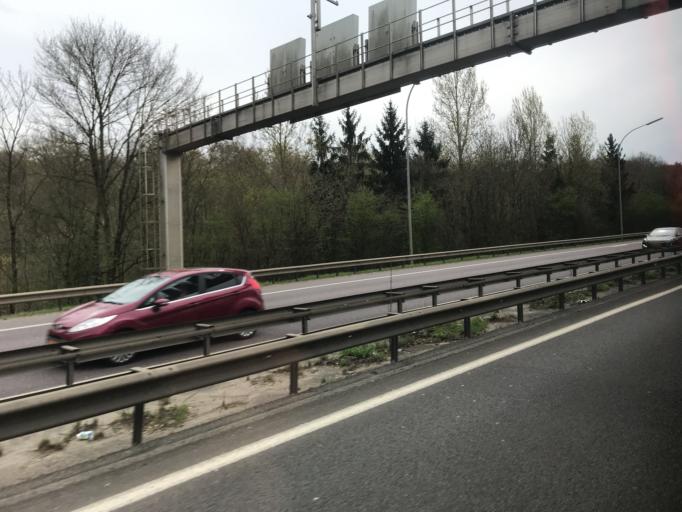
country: LU
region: Luxembourg
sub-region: Canton d'Esch-sur-Alzette
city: Leudelange
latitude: 49.5739
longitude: 6.0884
